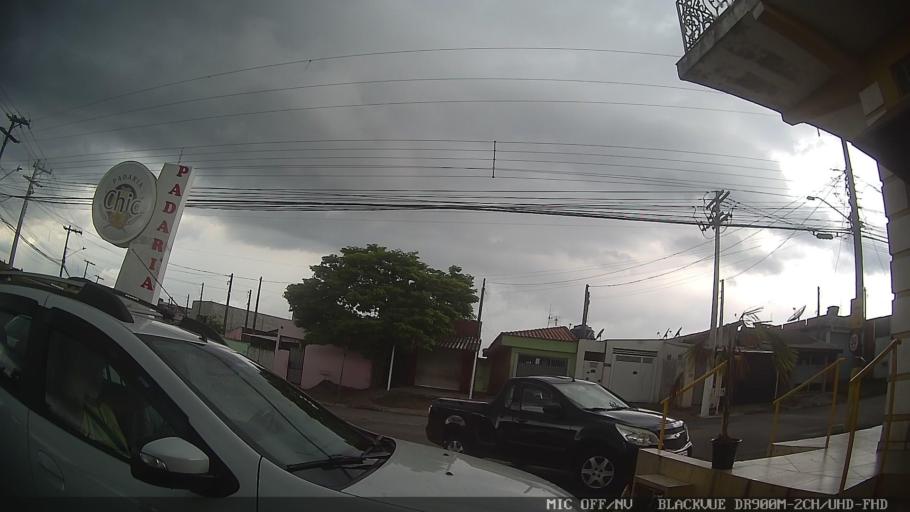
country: BR
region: Sao Paulo
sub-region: Atibaia
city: Atibaia
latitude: -23.1416
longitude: -46.5863
